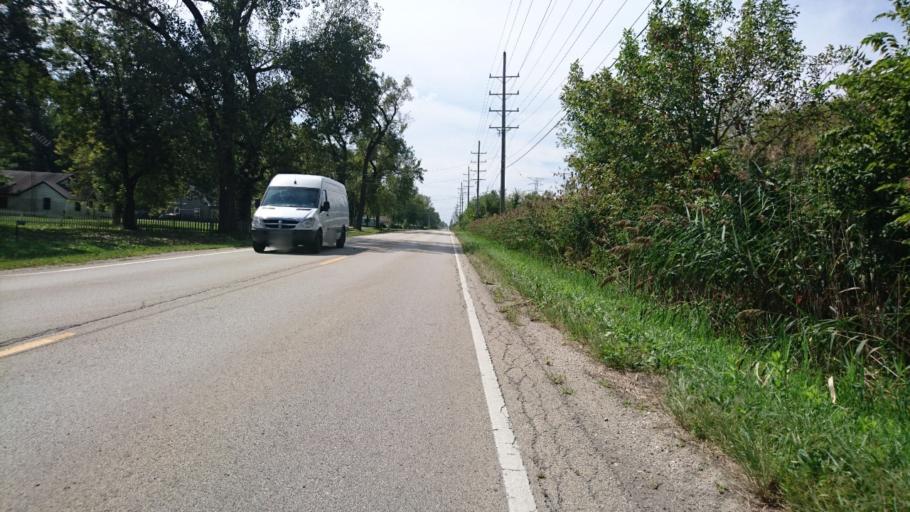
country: US
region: Illinois
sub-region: Will County
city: Wilmington
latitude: 41.3020
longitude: -88.1638
